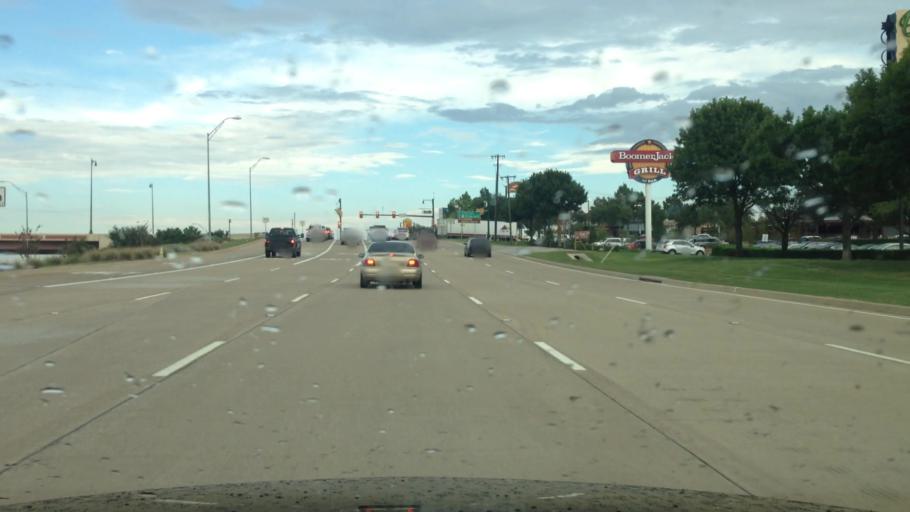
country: US
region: Texas
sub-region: Tarrant County
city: Grapevine
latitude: 32.9220
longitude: -97.0805
